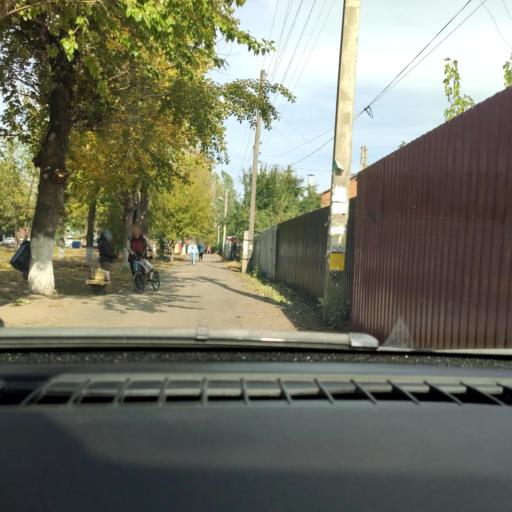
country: RU
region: Voronezj
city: Novaya Usman'
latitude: 51.6128
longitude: 39.3751
